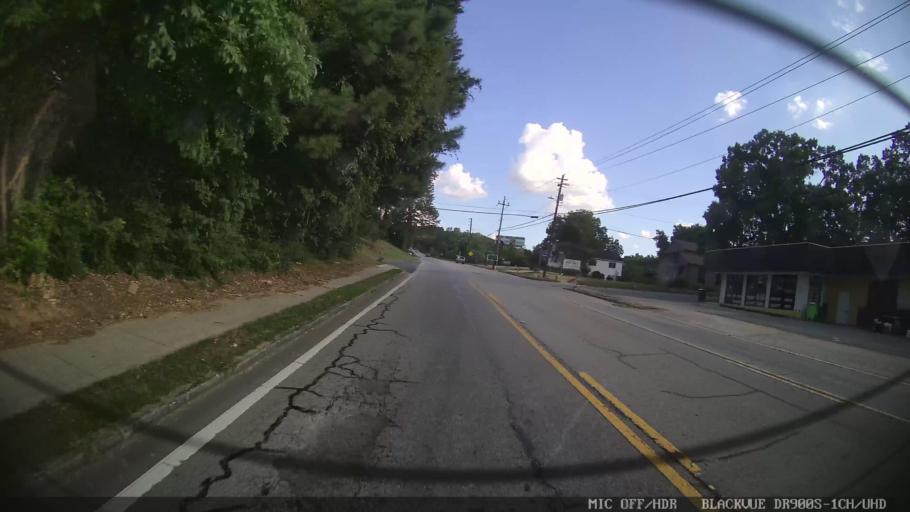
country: US
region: Georgia
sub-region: Floyd County
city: Rome
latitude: 34.2280
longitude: -85.1595
